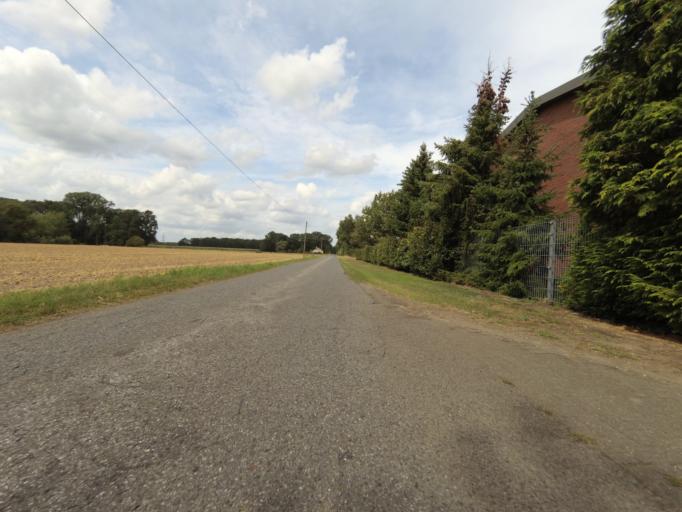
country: DE
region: North Rhine-Westphalia
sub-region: Regierungsbezirk Munster
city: Ahaus
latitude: 52.1313
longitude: 7.0048
